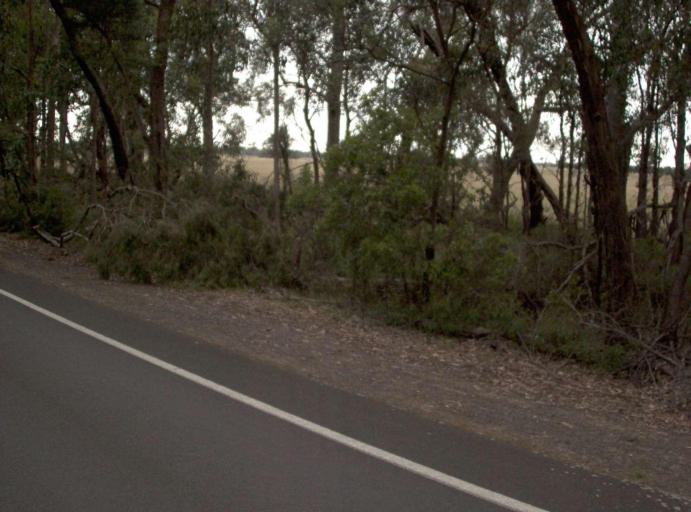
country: AU
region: Victoria
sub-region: Wellington
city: Sale
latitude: -38.4101
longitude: 146.9640
